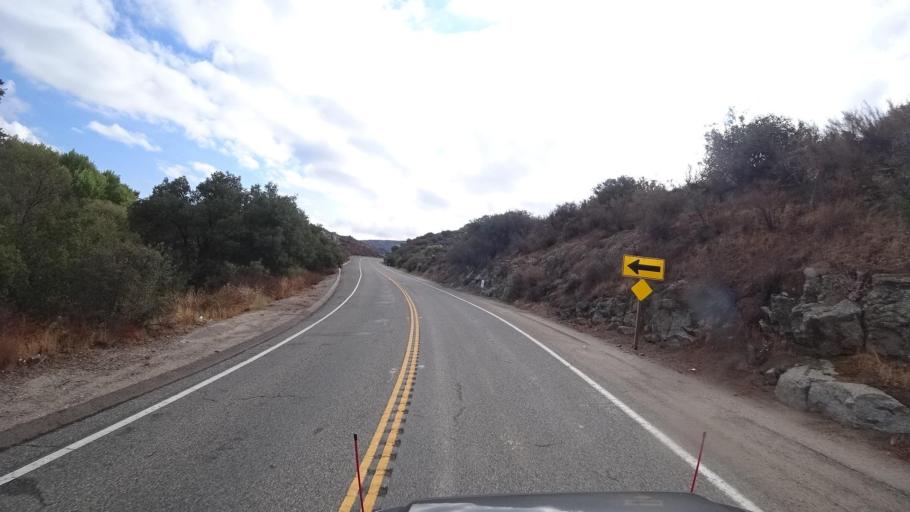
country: MX
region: Baja California
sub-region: Tecate
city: Hacienda Tecate
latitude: 32.5908
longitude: -116.5257
